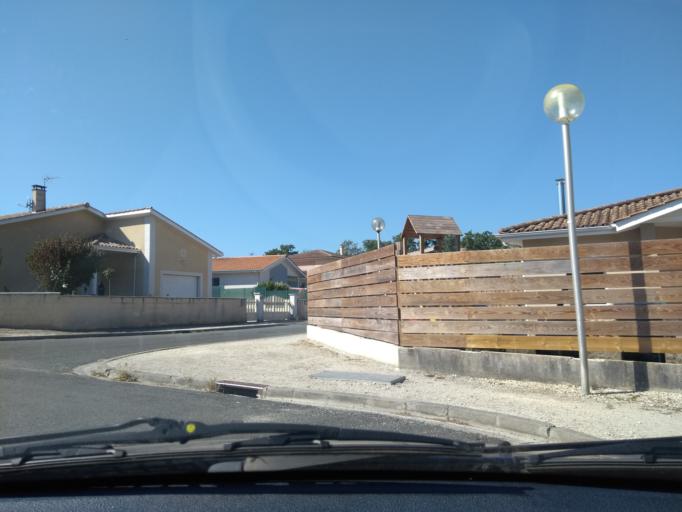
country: FR
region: Aquitaine
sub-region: Departement de la Gironde
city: Leognan
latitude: 44.7349
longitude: -0.6099
